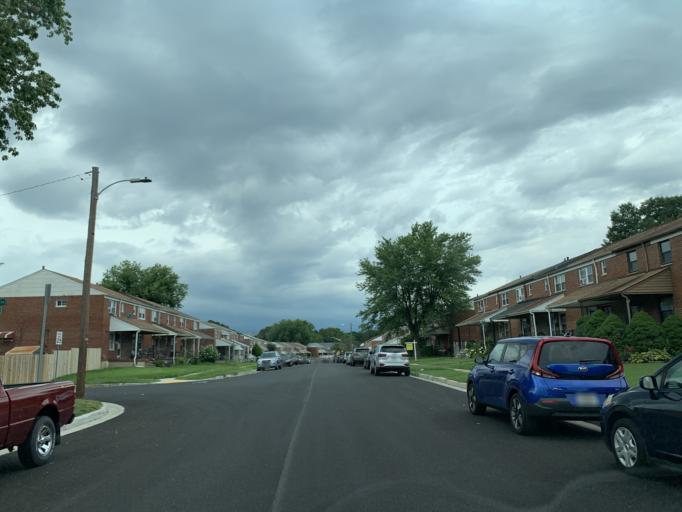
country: US
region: Maryland
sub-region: Baltimore County
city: Essex
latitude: 39.2972
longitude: -76.4531
